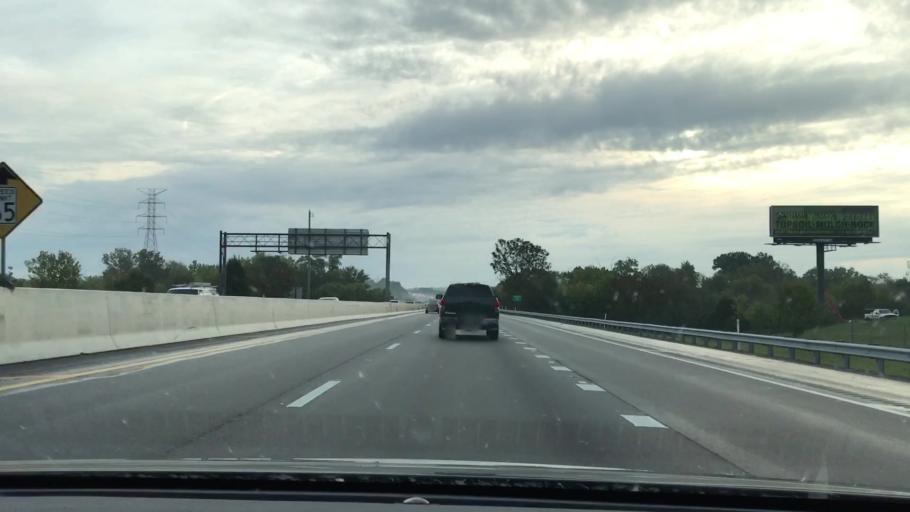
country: US
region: Tennessee
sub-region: Davidson County
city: Goodlettsville
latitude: 36.3121
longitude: -86.6753
